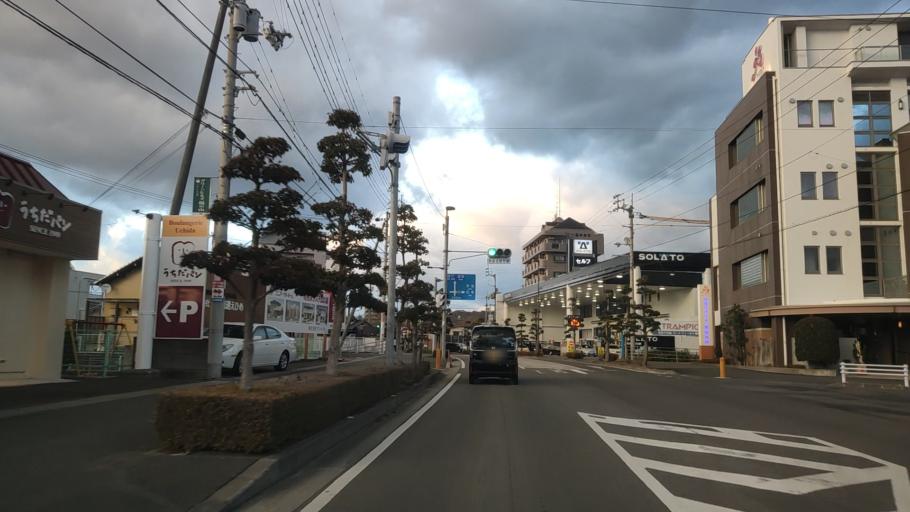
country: JP
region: Ehime
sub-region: Shikoku-chuo Shi
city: Matsuyama
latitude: 33.8372
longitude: 132.7868
